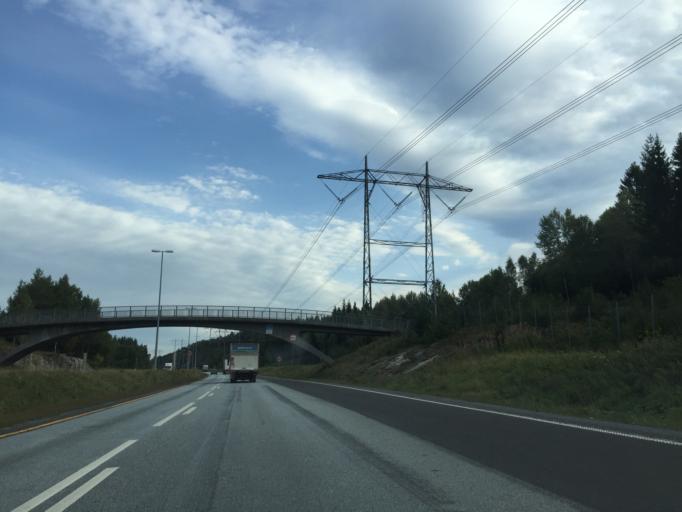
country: NO
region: Akershus
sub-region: Oppegard
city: Kolbotn
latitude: 59.7971
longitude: 10.8430
